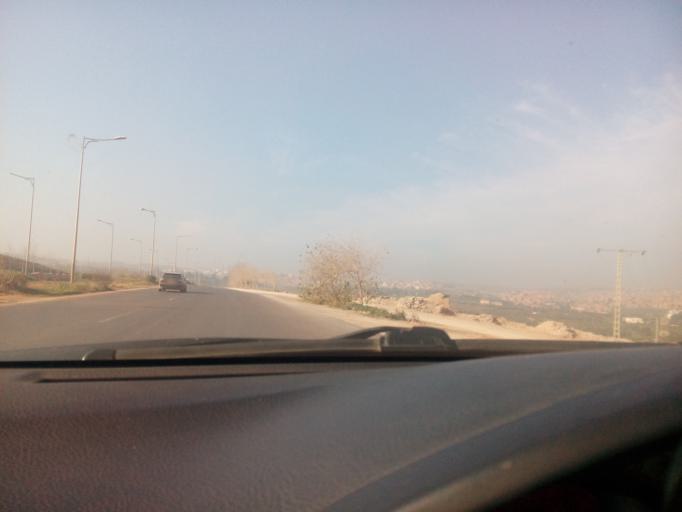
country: DZ
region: Oran
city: Oran
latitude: 35.6527
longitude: -0.6857
